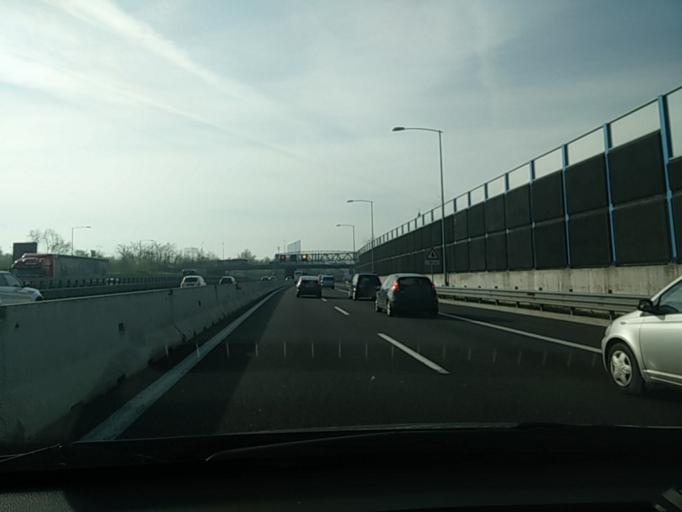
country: IT
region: Emilia-Romagna
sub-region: Provincia di Bologna
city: Quarto Inferiore
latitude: 44.5115
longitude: 11.3796
